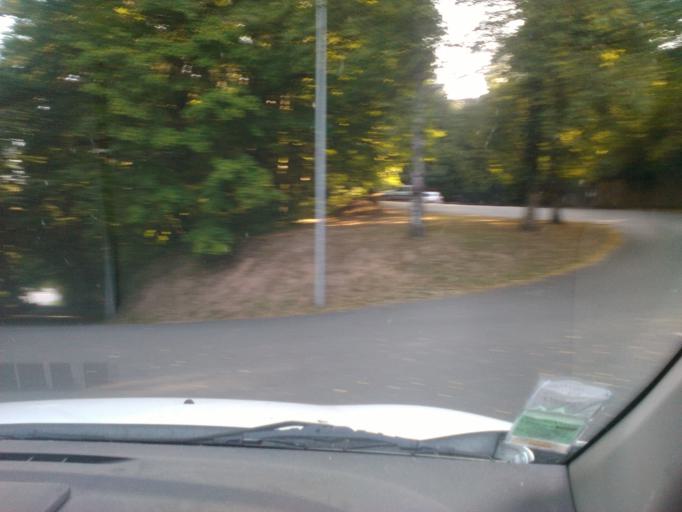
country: FR
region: Lorraine
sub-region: Departement des Vosges
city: Epinal
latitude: 48.1761
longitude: 6.4558
